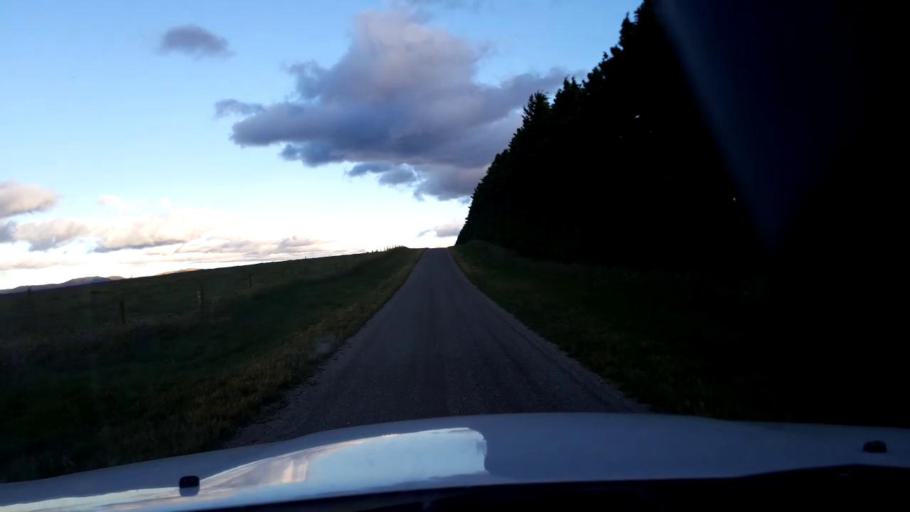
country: NZ
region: Canterbury
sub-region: Timaru District
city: Pleasant Point
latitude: -44.2623
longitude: 170.9181
